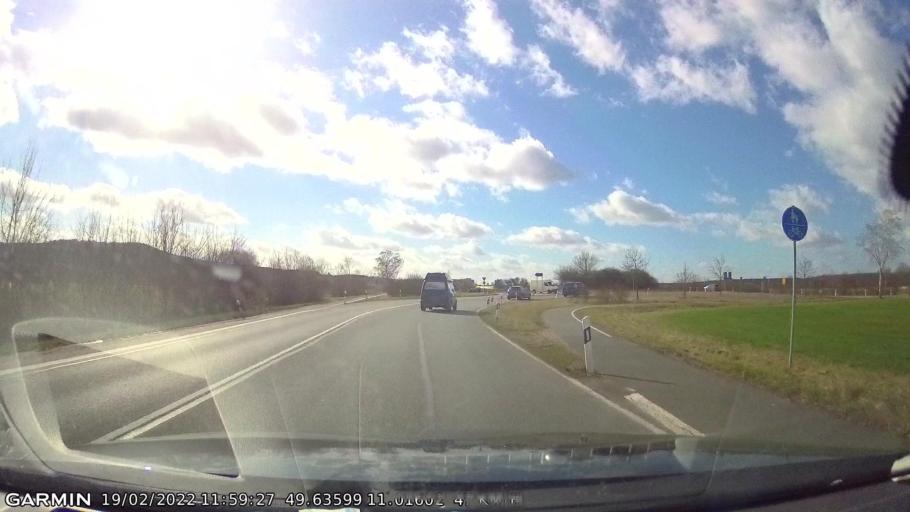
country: DE
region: Bavaria
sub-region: Regierungsbezirk Mittelfranken
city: Bubenreuth
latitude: 49.6361
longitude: 11.0176
